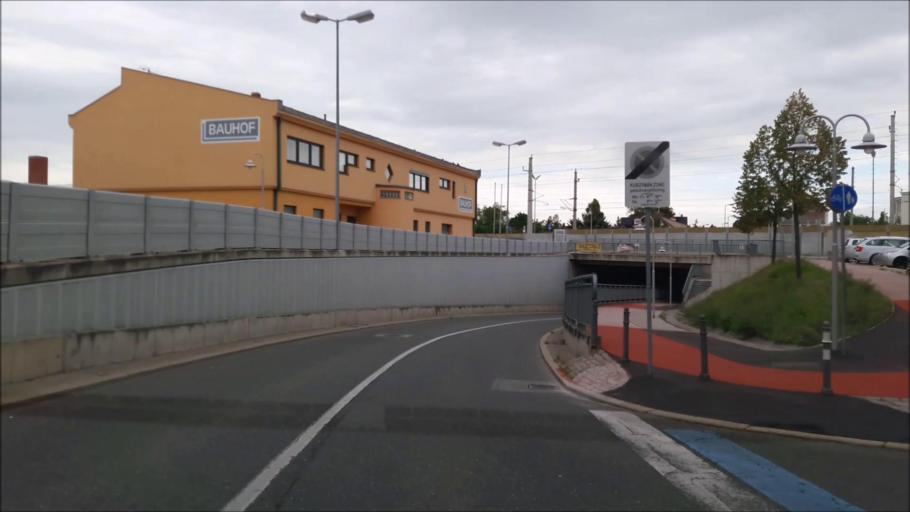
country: AT
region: Lower Austria
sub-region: Politischer Bezirk Wien-Umgebung
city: Schwechat
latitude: 48.1447
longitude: 16.4786
